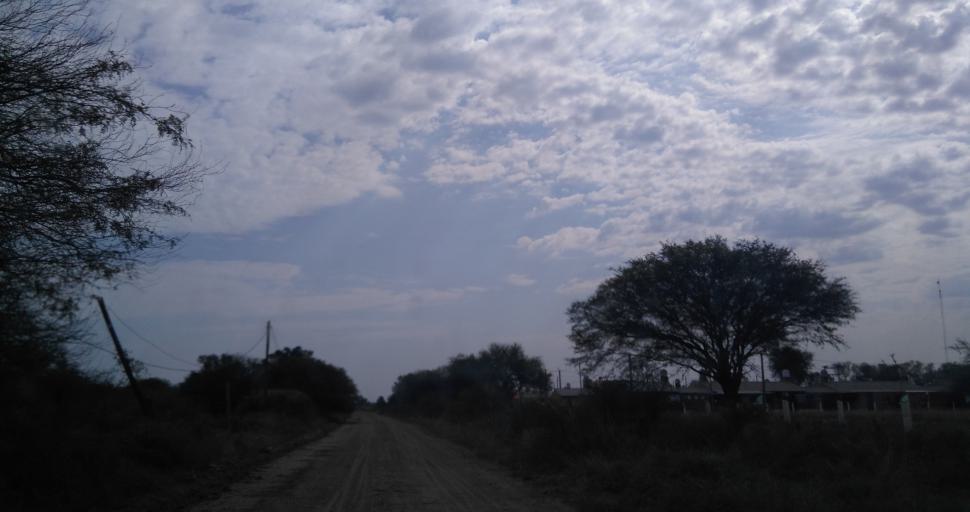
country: AR
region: Chaco
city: Fontana
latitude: -27.4594
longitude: -59.0490
